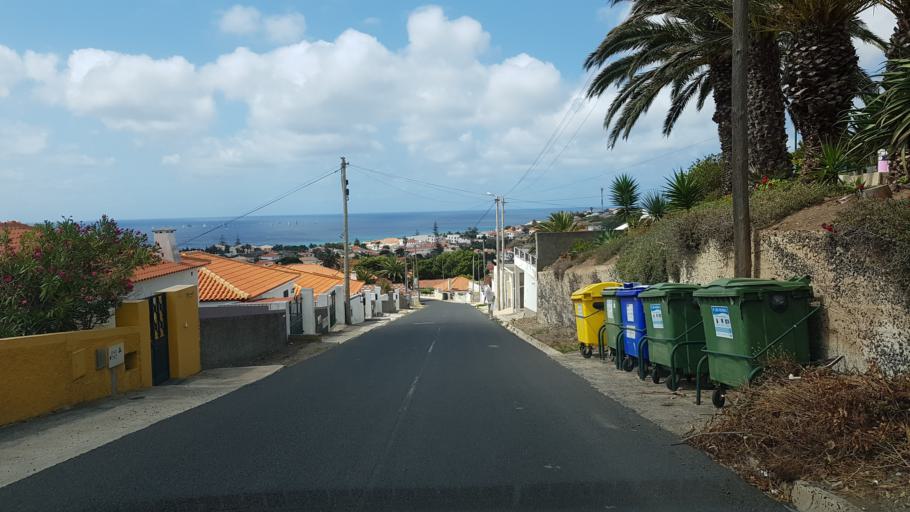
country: PT
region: Madeira
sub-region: Porto Santo
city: Vila de Porto Santo
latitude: 33.0671
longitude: -16.3332
